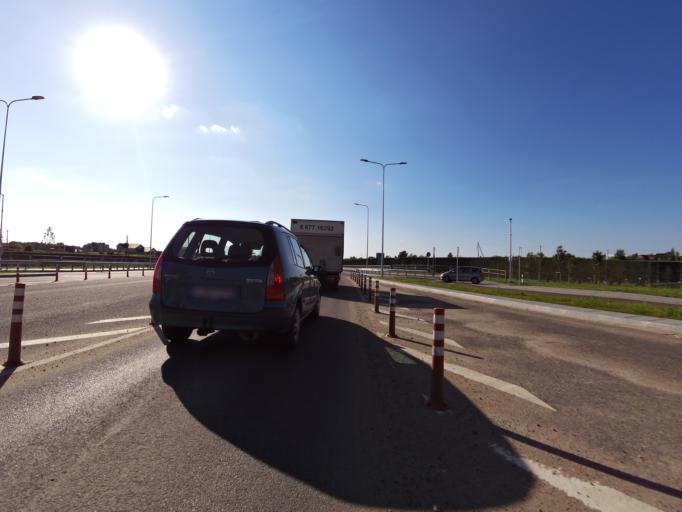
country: LT
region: Vilnius County
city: Justiniskes
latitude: 54.7247
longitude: 25.2091
